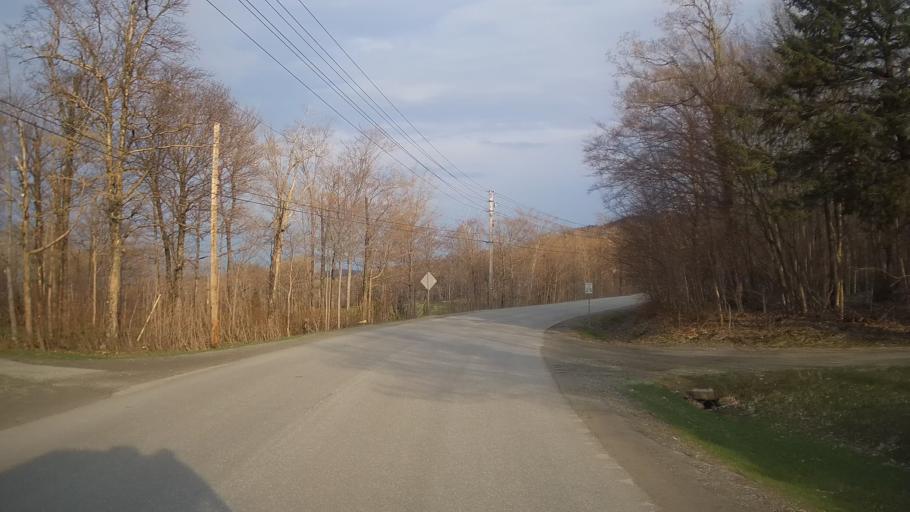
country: US
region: Vermont
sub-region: Franklin County
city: Richford
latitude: 44.9379
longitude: -72.5010
